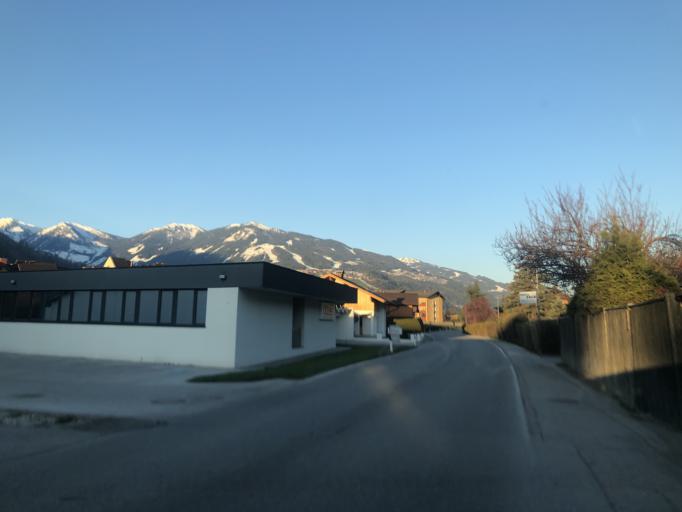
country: AT
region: Styria
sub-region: Politischer Bezirk Liezen
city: Schladming
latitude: 47.4006
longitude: 13.6983
